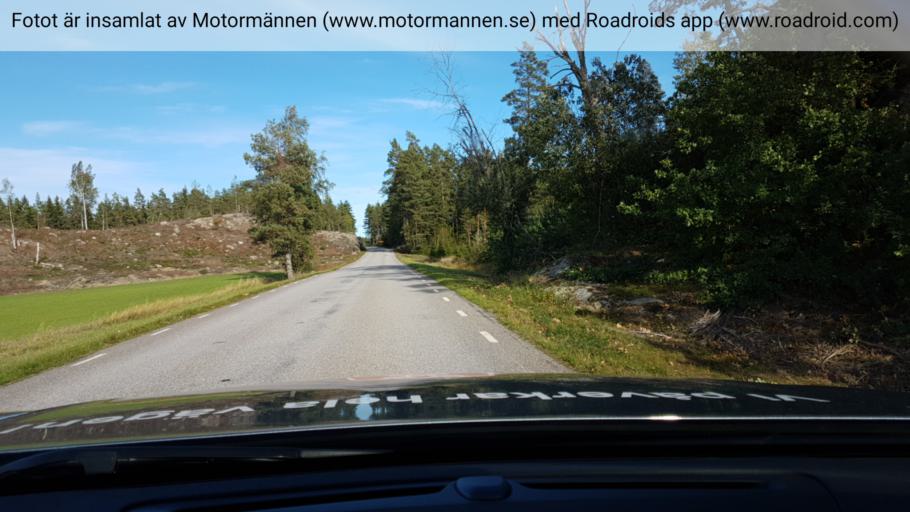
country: SE
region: OEstergoetland
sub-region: Valdemarsviks Kommun
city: Valdemarsvik
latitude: 58.0606
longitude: 16.6300
